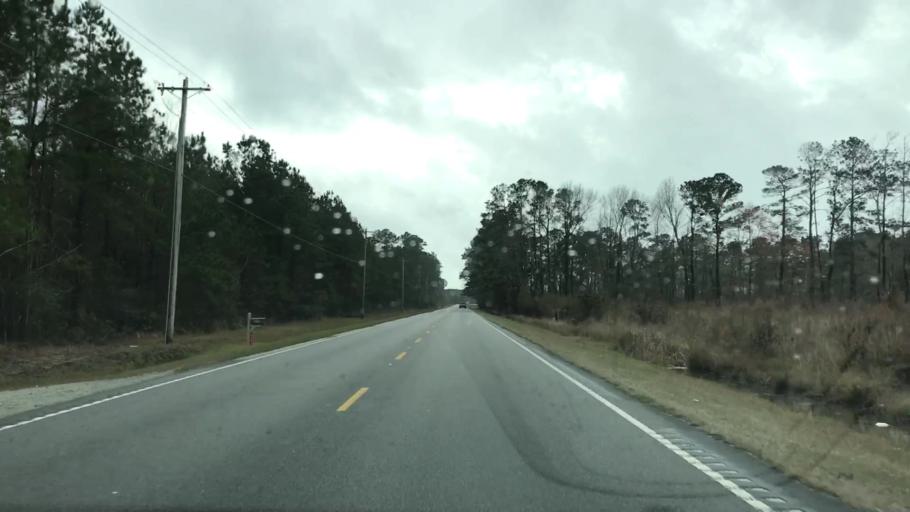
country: US
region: South Carolina
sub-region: Horry County
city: Socastee
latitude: 33.7317
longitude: -79.0832
